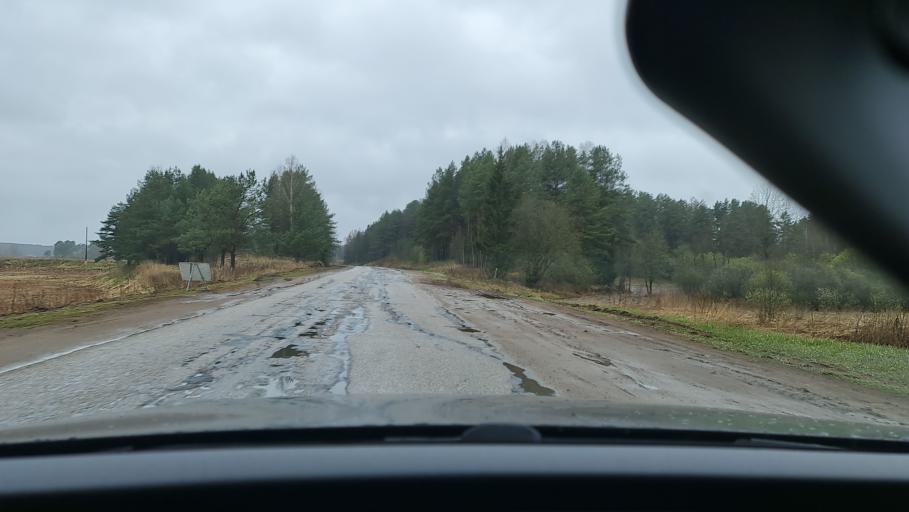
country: RU
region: Novgorod
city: Valday
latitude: 58.0398
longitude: 32.9276
